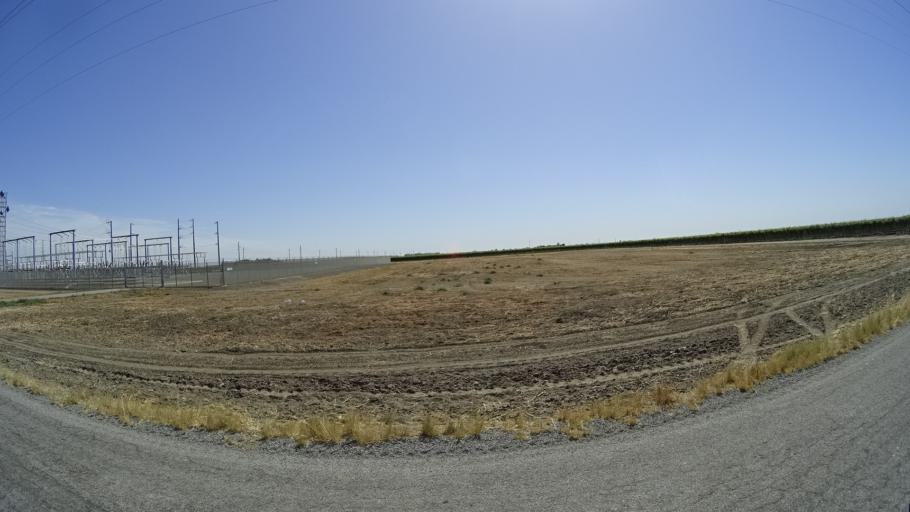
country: US
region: California
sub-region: Kings County
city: Stratford
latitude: 36.2395
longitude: -119.8345
